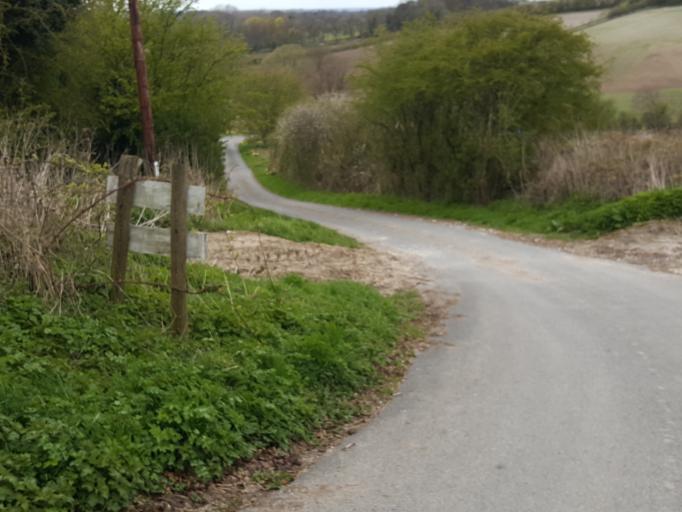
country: GB
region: England
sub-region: East Riding of Yorkshire
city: South Cave
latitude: 53.7732
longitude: -0.5865
